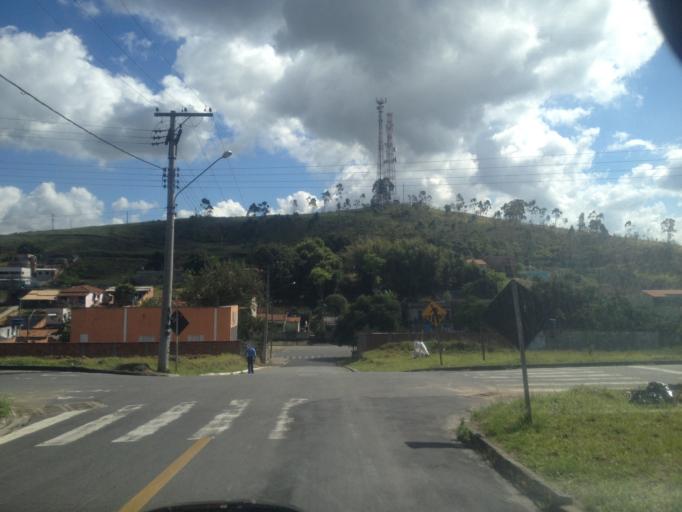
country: BR
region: Rio de Janeiro
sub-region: Porto Real
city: Porto Real
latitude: -22.4414
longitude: -44.3208
